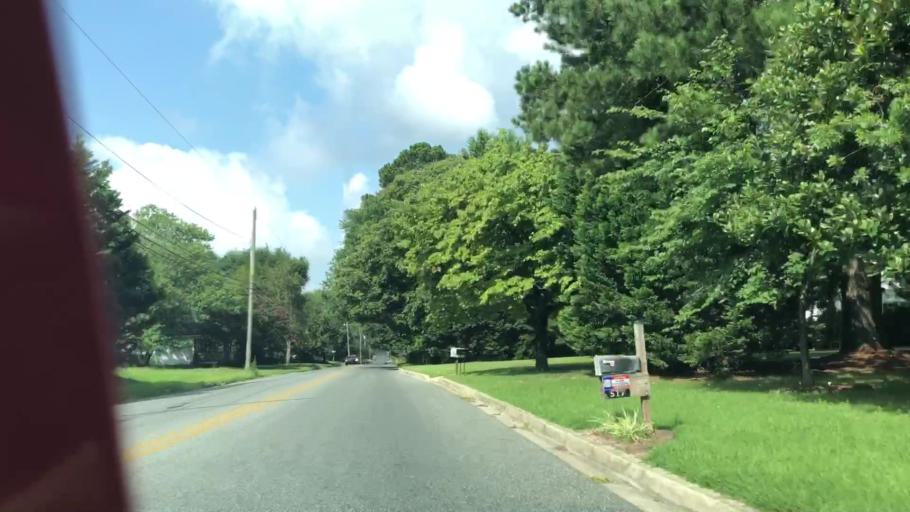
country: US
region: Maryland
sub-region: Wicomico County
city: Salisbury
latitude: 38.3936
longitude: -75.5680
